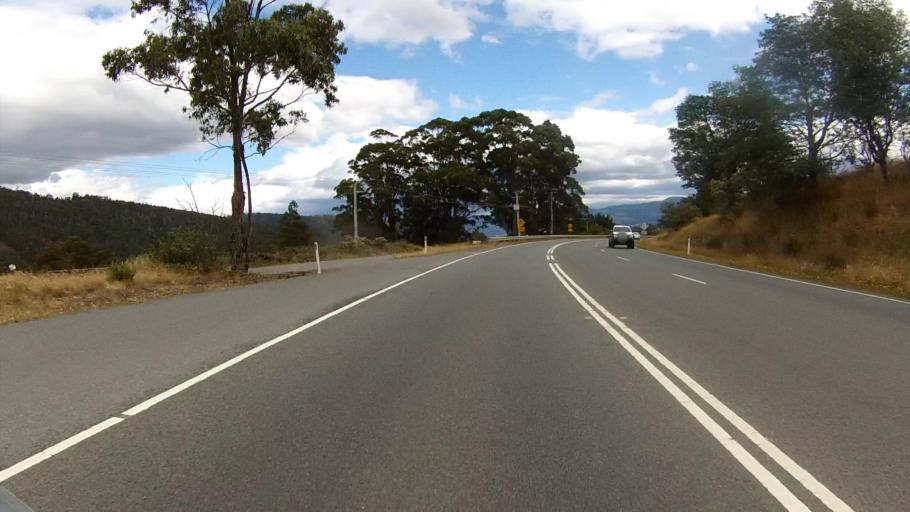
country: AU
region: Tasmania
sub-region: Huon Valley
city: Huonville
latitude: -42.9770
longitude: 147.1544
